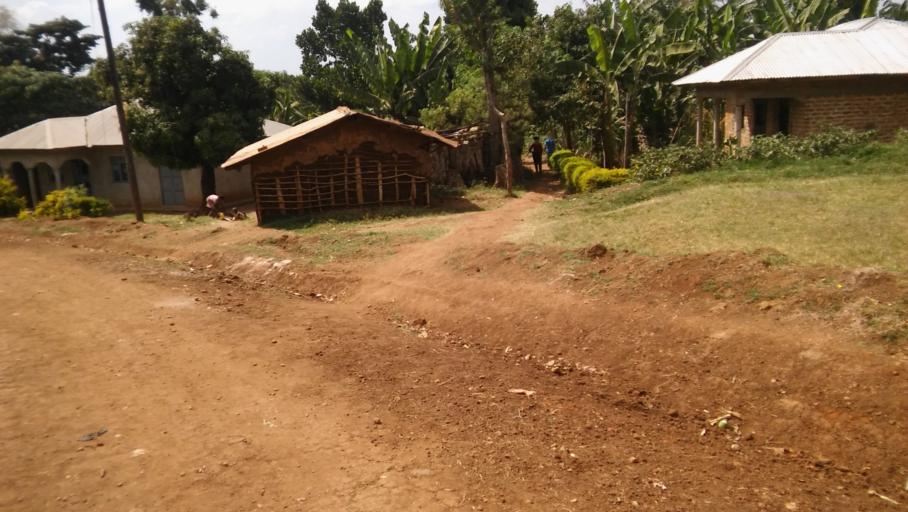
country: UG
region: Eastern Region
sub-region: Mbale District
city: Mbale
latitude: 1.0576
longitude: 34.2160
